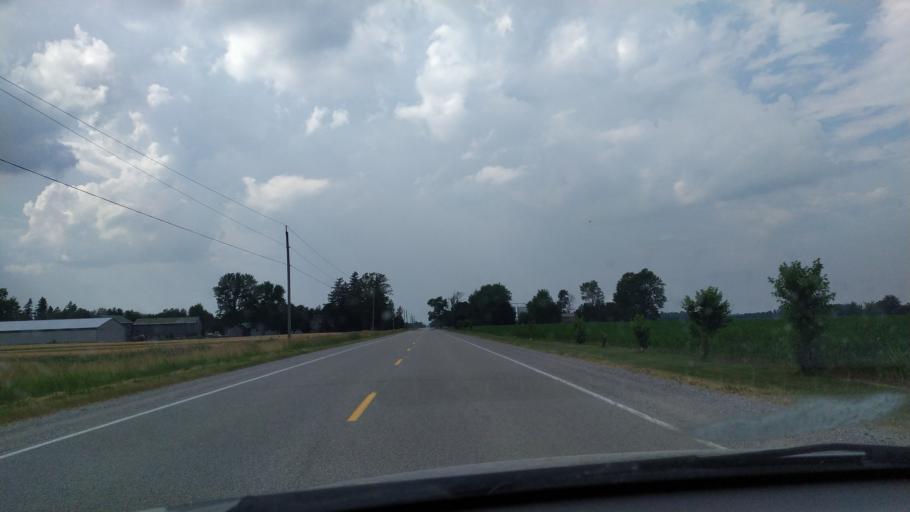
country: CA
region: Ontario
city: Dorchester
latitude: 43.1779
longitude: -81.1410
